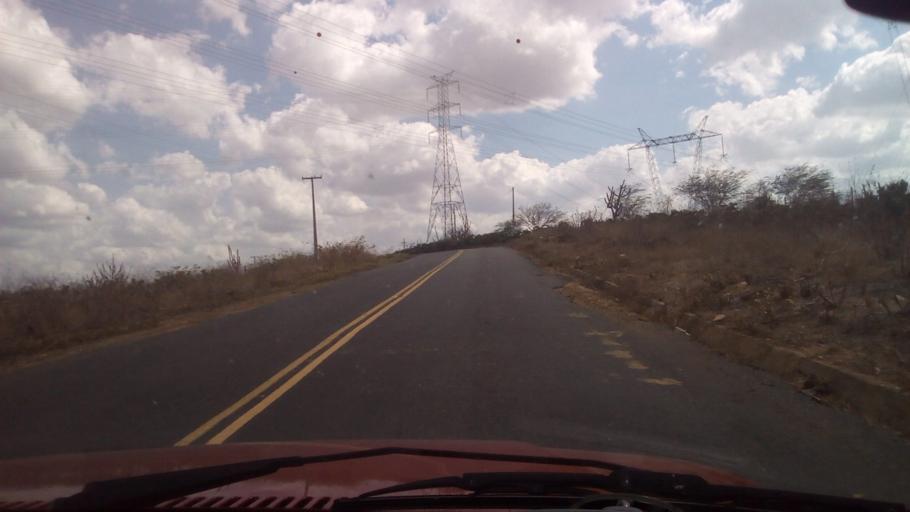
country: BR
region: Paraiba
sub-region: Cacimba De Dentro
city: Cacimba de Dentro
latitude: -6.7066
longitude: -35.7271
